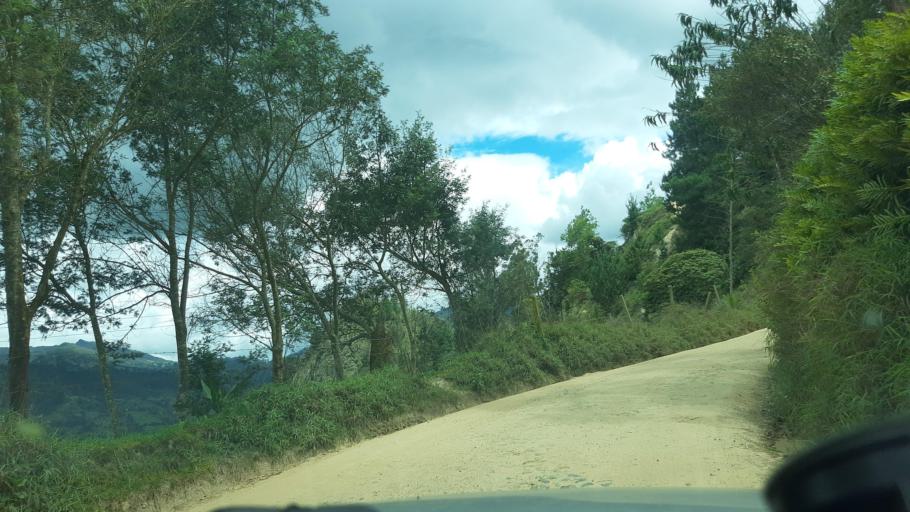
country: CO
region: Cundinamarca
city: Umbita
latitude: 5.2196
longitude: -73.4427
